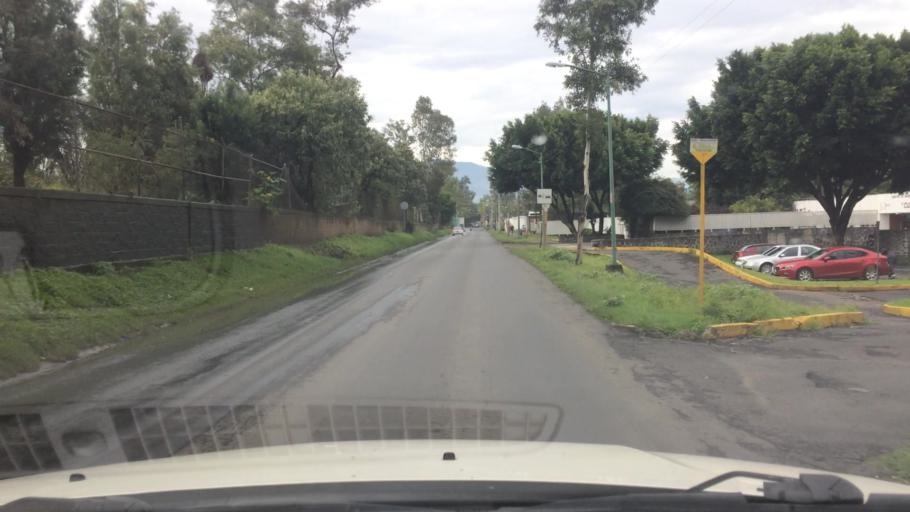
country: MX
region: Mexico City
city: Xochimilco
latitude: 19.3031
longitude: -99.1006
